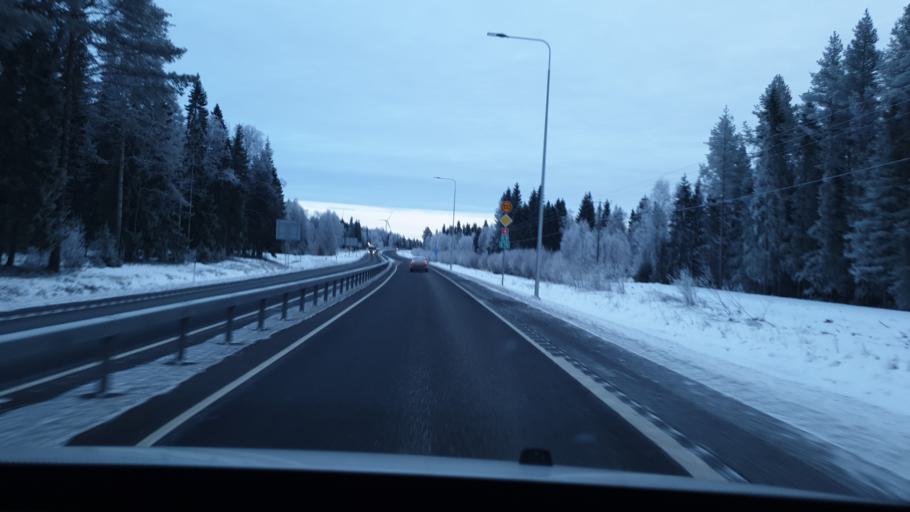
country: FI
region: Lapland
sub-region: Kemi-Tornio
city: Simo
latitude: 65.6685
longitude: 24.9422
